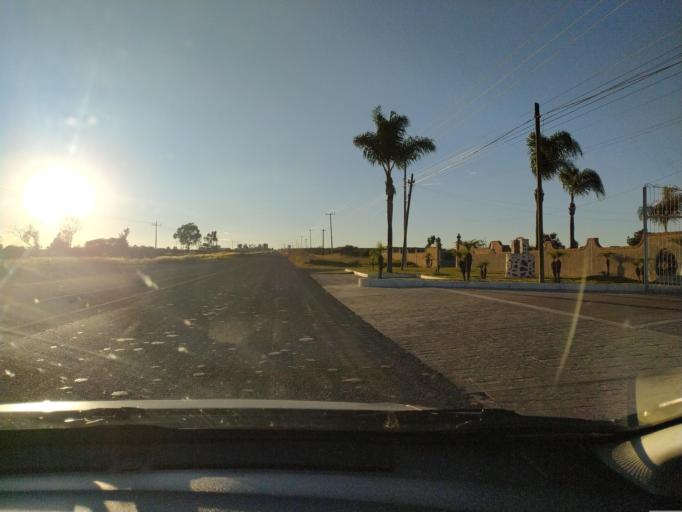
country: MX
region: Jalisco
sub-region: San Julian
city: Colonia Veintitres de Mayo
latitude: 21.0125
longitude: -102.1990
